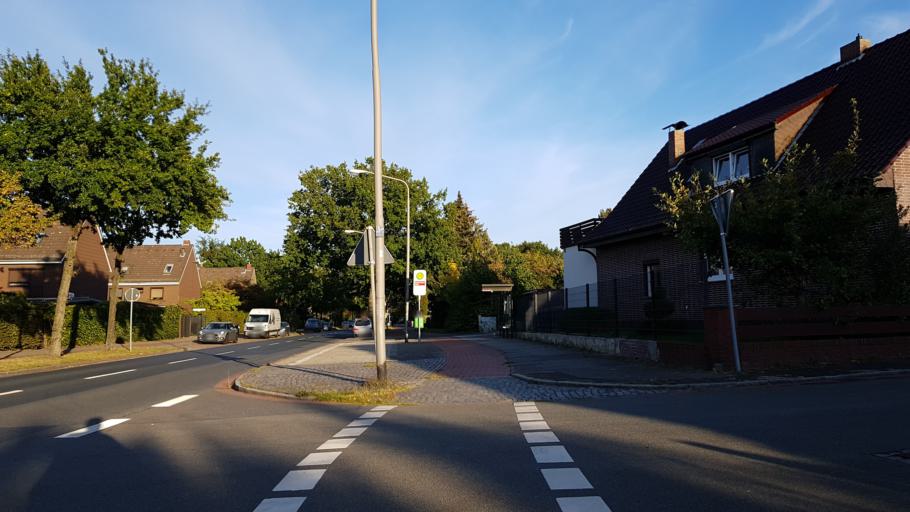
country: DE
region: Lower Saxony
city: Riede
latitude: 53.0443
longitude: 8.9223
